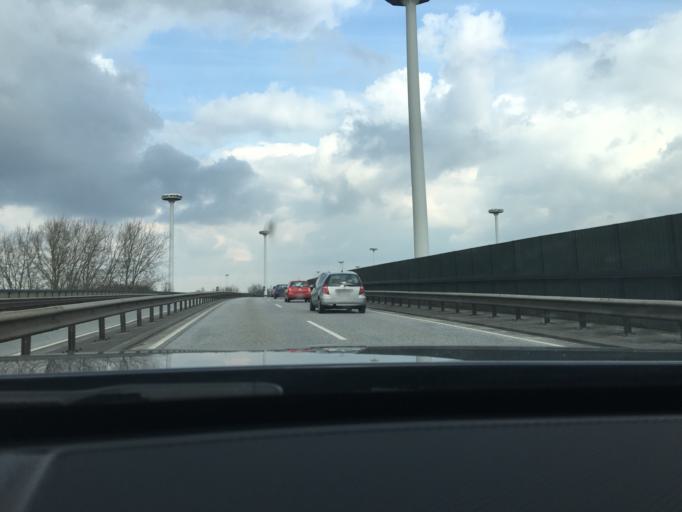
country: DE
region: Bremen
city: Bremen
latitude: 53.0830
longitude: 8.7926
